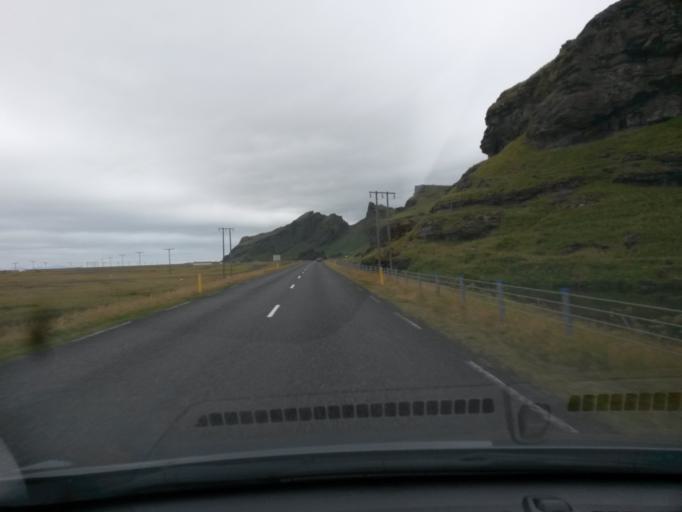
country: IS
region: South
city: Vestmannaeyjar
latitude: 63.5218
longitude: -19.5266
